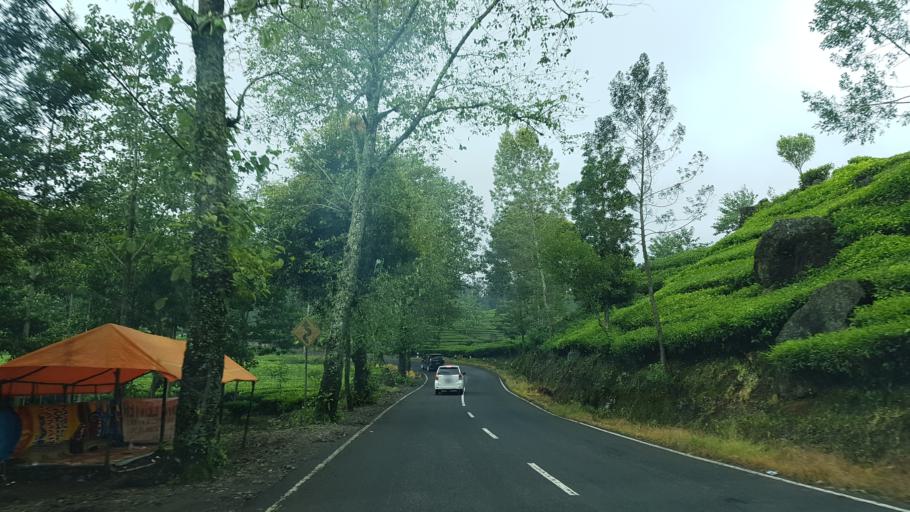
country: ID
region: West Java
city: Banjar
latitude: -7.1507
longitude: 107.3769
